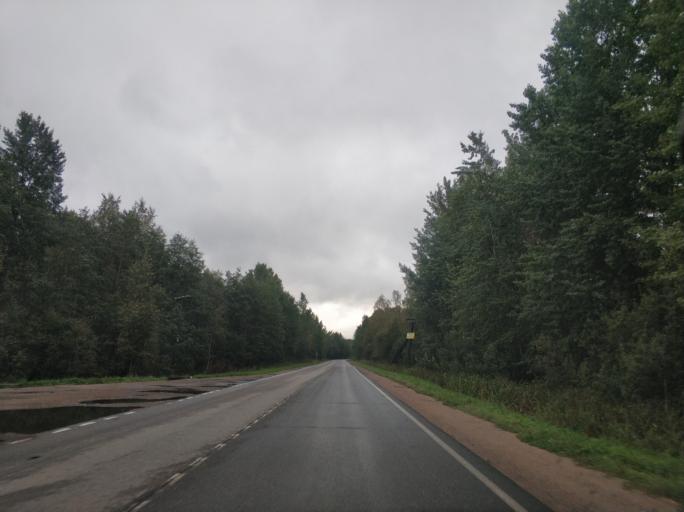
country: RU
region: Leningrad
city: Borisova Griva
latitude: 60.1187
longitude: 30.9636
